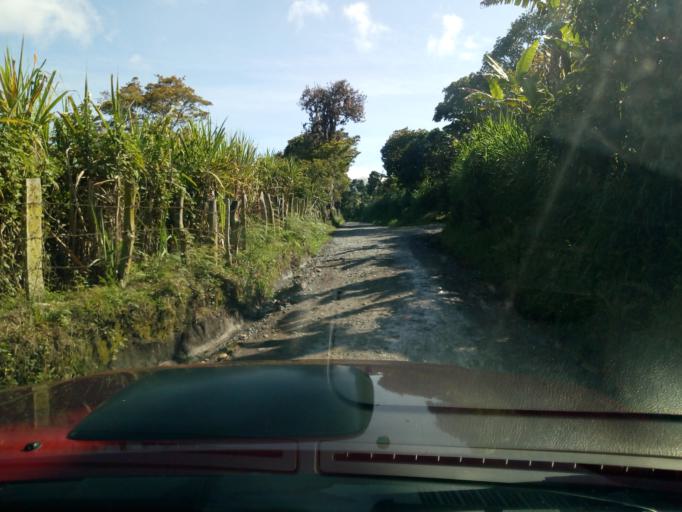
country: CO
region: Boyaca
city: Moniquira
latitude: 5.8854
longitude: -73.5391
